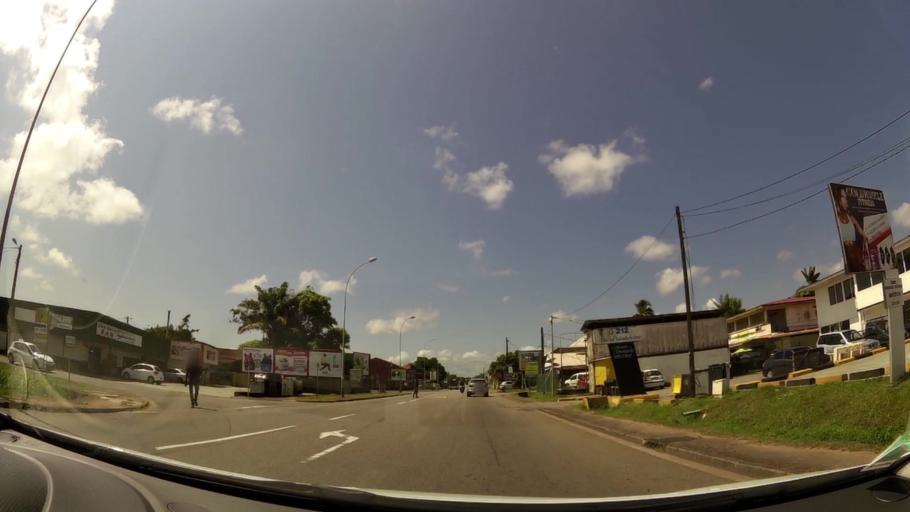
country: GF
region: Guyane
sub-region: Guyane
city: Cayenne
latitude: 4.9304
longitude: -52.3261
